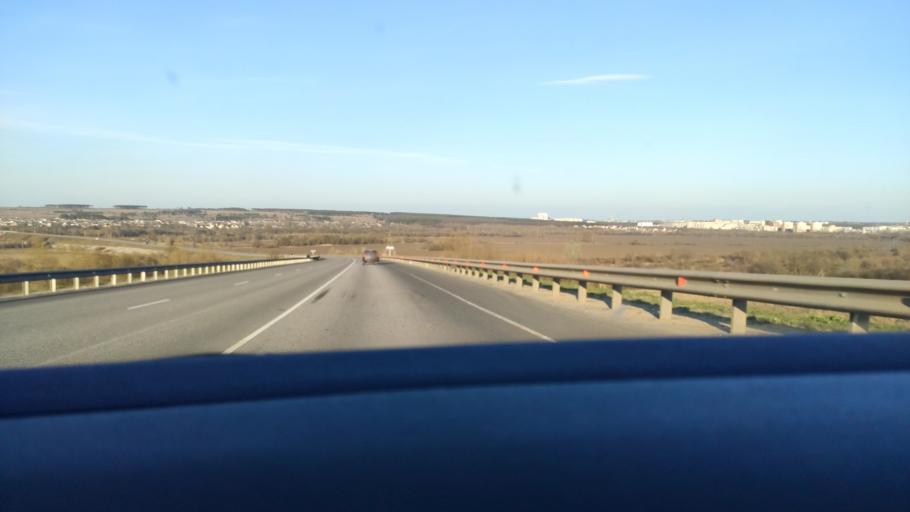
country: RU
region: Voronezj
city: Kolodeznyy
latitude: 51.3280
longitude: 39.1537
